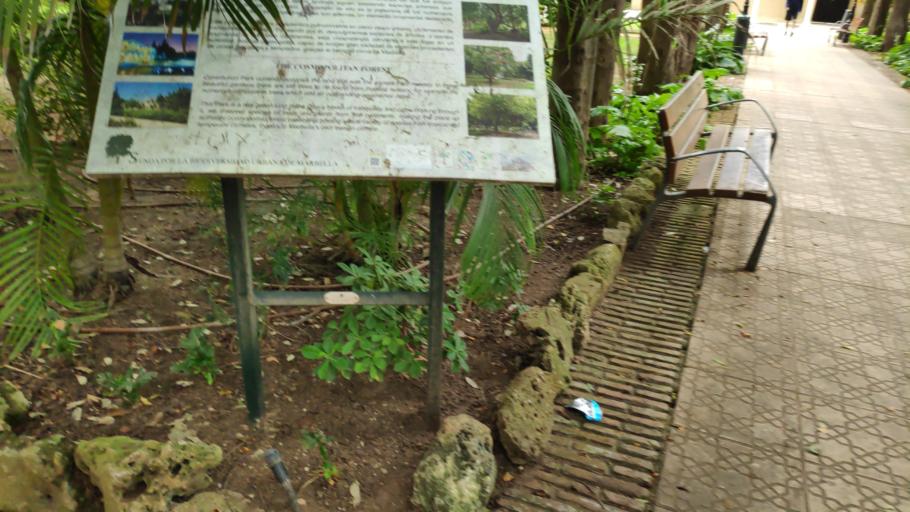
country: ES
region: Andalusia
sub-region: Provincia de Malaga
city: Marbella
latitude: 36.5073
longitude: -4.8911
